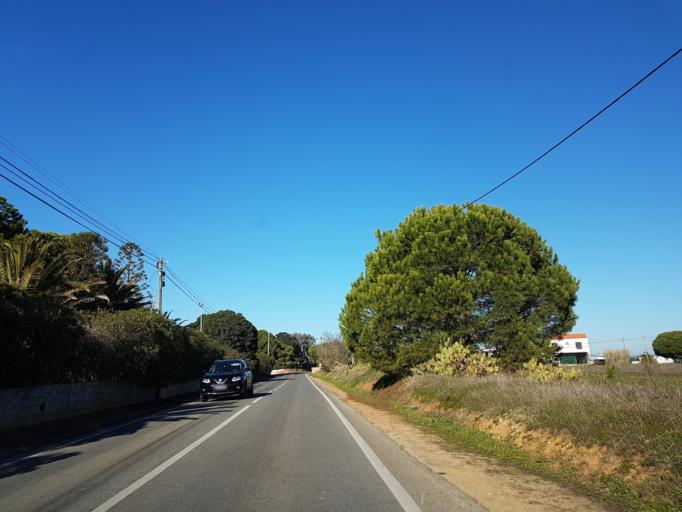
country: PT
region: Faro
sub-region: Lagoa
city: Carvoeiro
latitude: 37.0995
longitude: -8.4427
